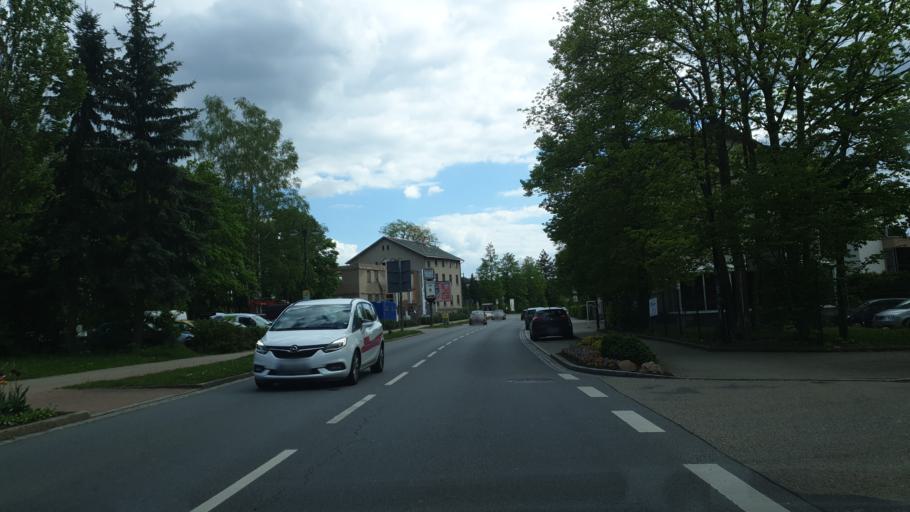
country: DE
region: Saxony
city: Lugau
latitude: 50.7411
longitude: 12.7467
